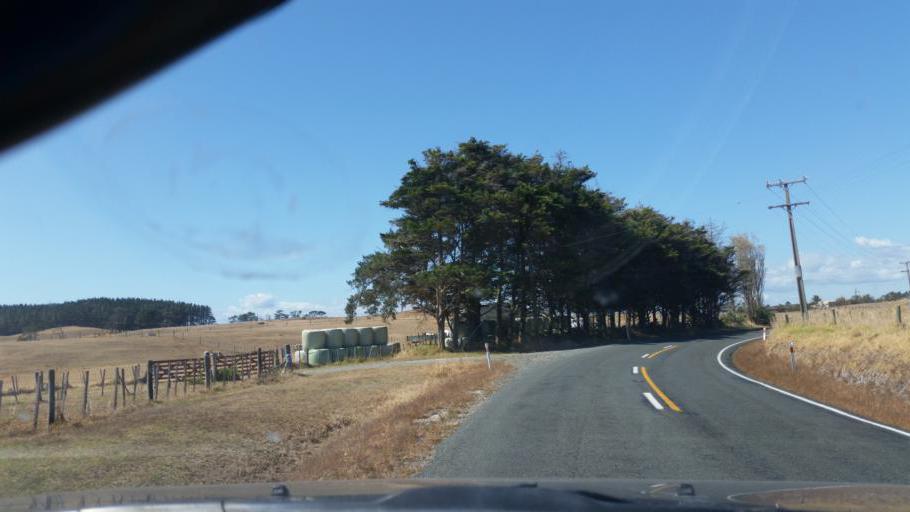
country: NZ
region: Northland
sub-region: Kaipara District
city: Dargaville
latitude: -35.9460
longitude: 173.8119
